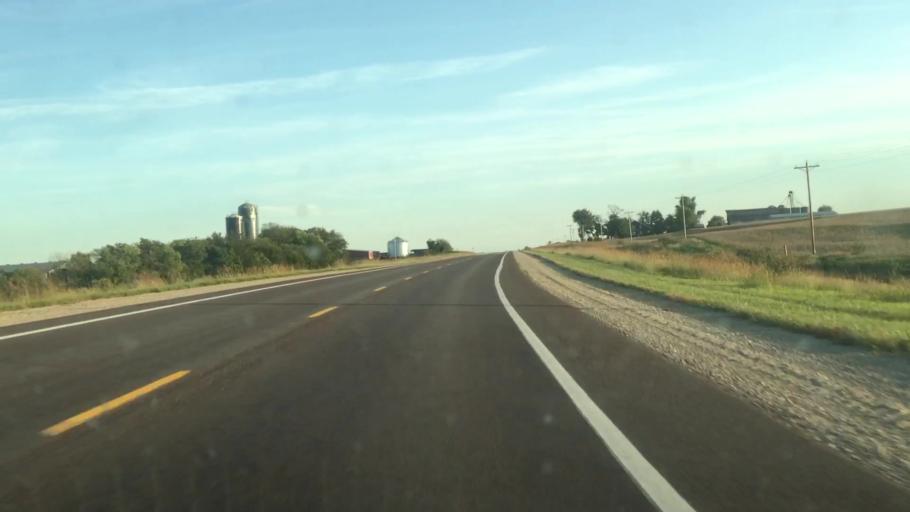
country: US
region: Kansas
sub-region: Atchison County
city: Atchison
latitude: 39.4451
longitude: -95.0936
